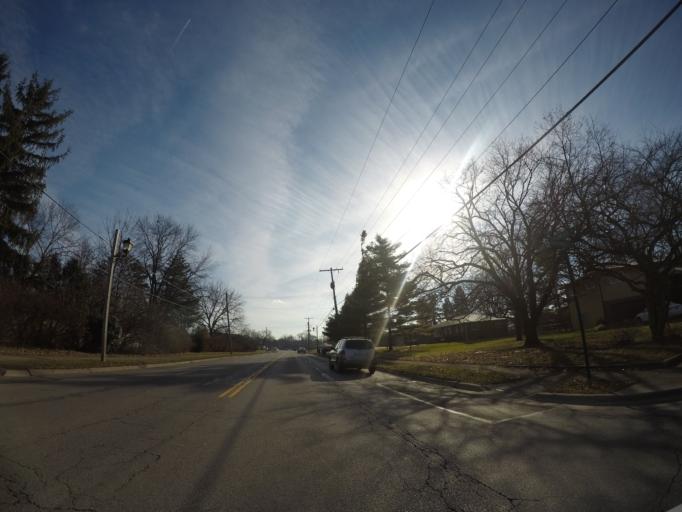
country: US
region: Ohio
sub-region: Franklin County
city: Upper Arlington
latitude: 40.0265
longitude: -83.0595
